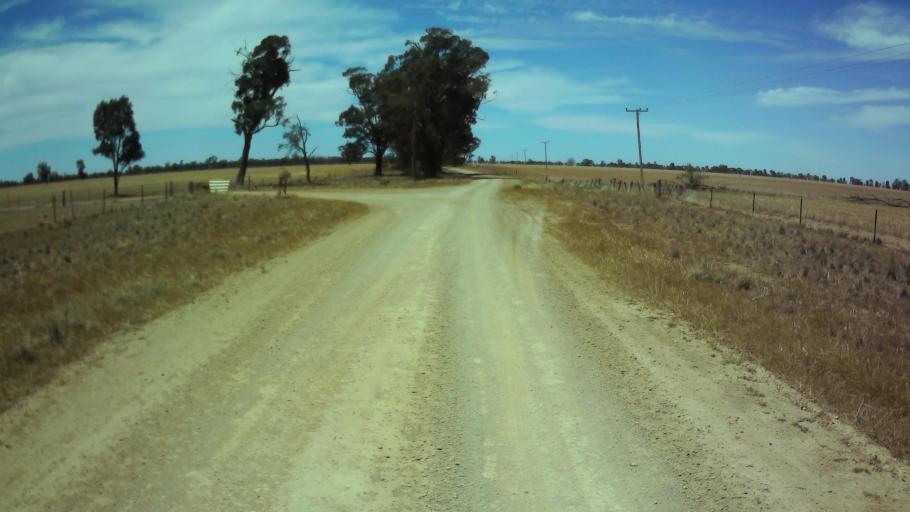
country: AU
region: New South Wales
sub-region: Weddin
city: Grenfell
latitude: -33.8879
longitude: 147.8032
